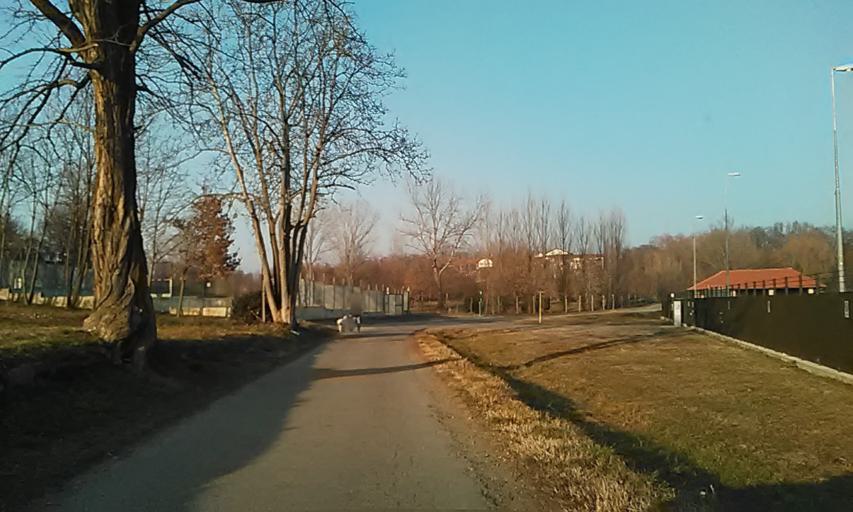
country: IT
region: Piedmont
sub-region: Provincia di Biella
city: Dorzano
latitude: 45.4142
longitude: 8.1033
